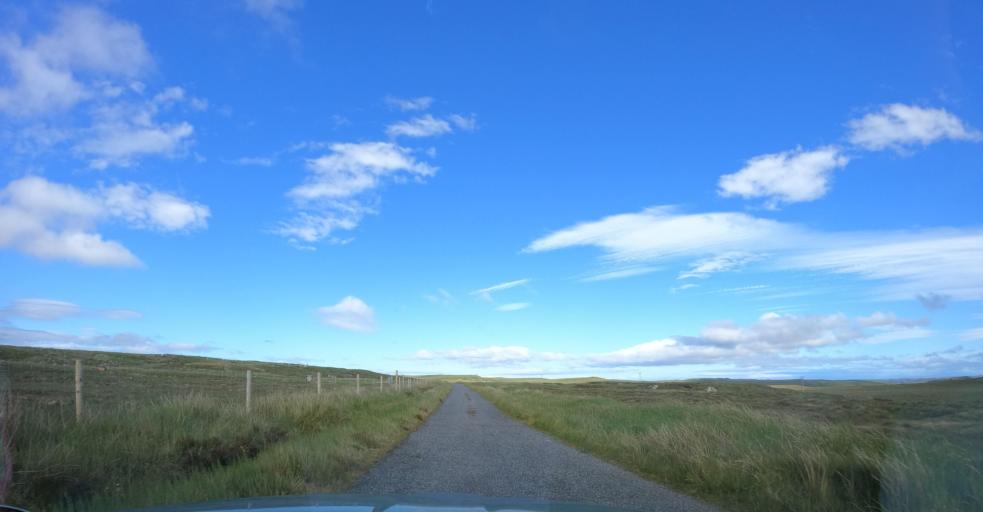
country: GB
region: Scotland
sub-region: Eilean Siar
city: Stornoway
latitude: 58.1732
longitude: -6.5633
